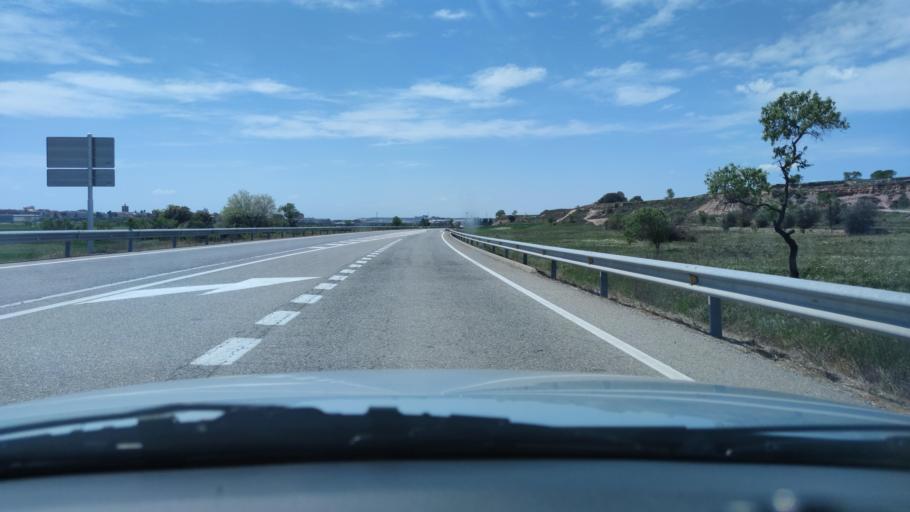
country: ES
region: Catalonia
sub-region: Provincia de Lleida
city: Tora de Riubregos
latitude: 41.7963
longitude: 1.3010
